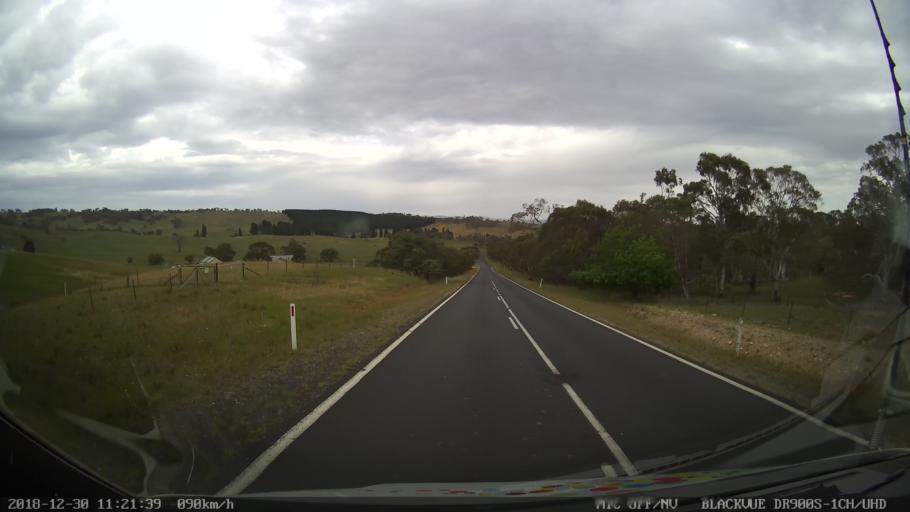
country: AU
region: New South Wales
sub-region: Snowy River
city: Jindabyne
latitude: -36.5085
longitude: 148.6754
